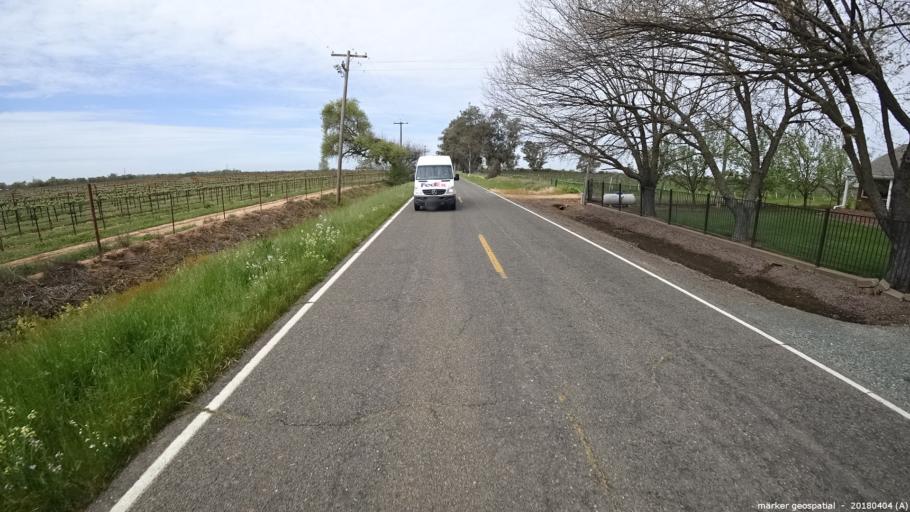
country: US
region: California
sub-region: Sacramento County
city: Herald
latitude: 38.2636
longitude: -121.1782
